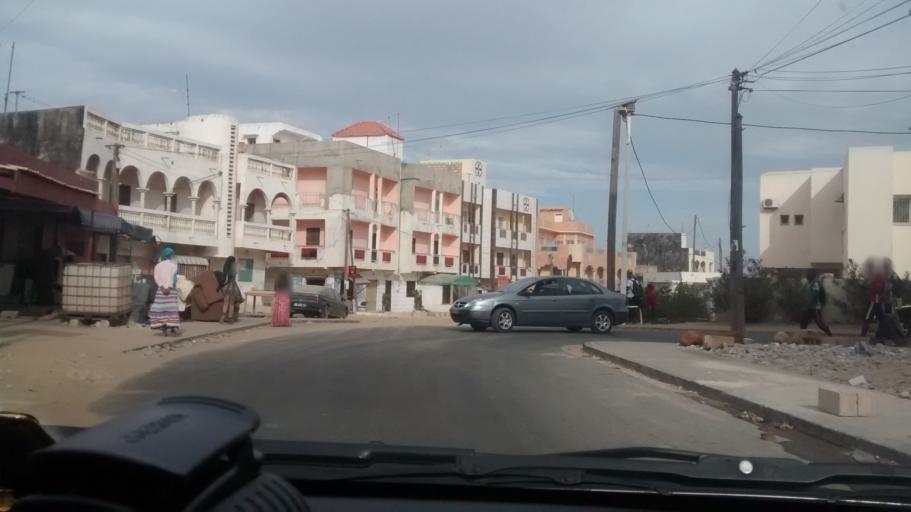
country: SN
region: Dakar
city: Pikine
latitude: 14.7629
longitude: -17.4184
